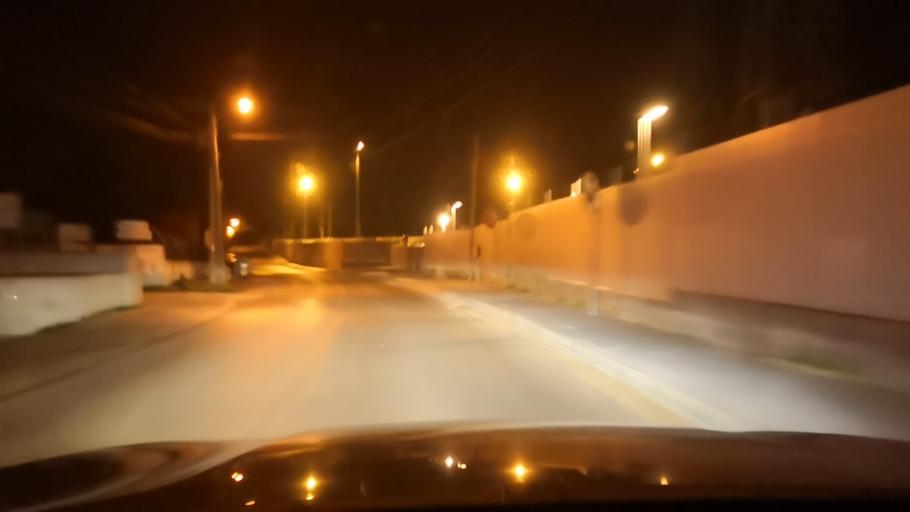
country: PT
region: Setubal
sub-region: Setubal
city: Setubal
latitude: 38.5444
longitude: -8.8788
